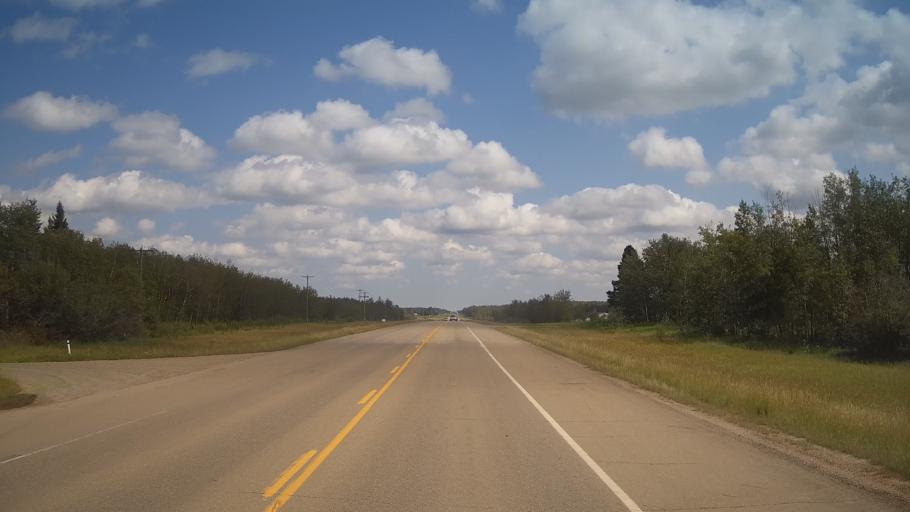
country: CA
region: Alberta
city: Sherwood Park
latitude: 53.3957
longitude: -113.0870
